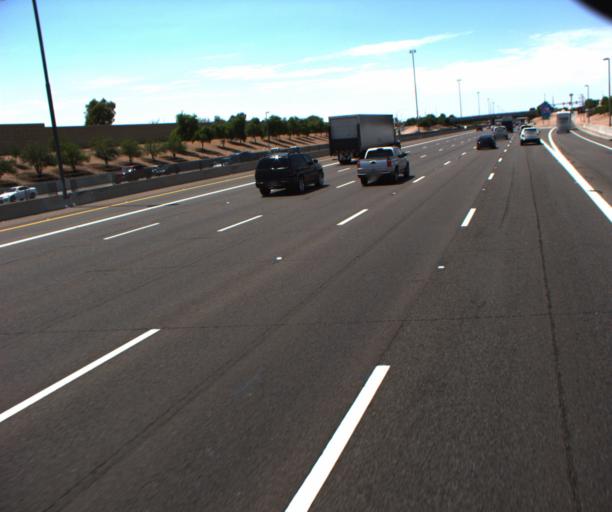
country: US
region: Arizona
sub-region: Maricopa County
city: Gilbert
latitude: 33.3865
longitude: -111.7826
